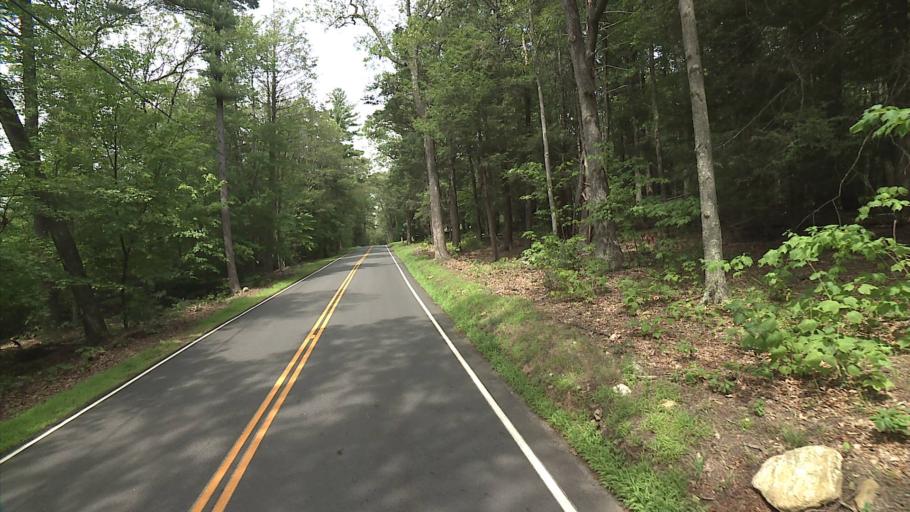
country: US
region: Massachusetts
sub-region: Hampden County
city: Holland
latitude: 41.9774
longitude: -72.1140
